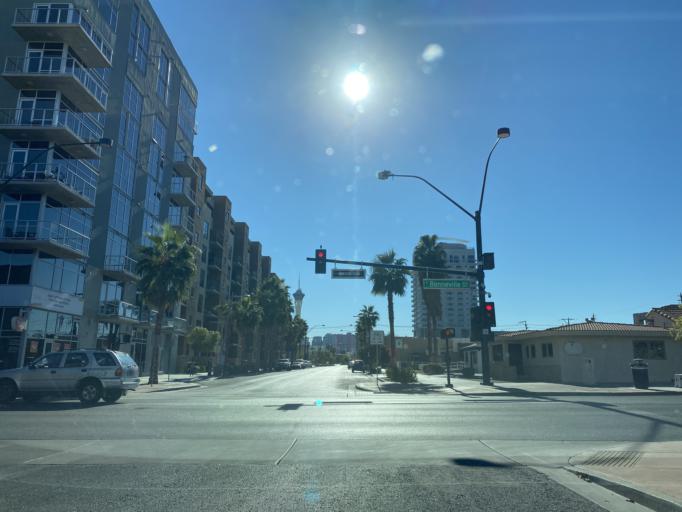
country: US
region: Nevada
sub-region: Clark County
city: Las Vegas
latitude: 36.1646
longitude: -115.1467
